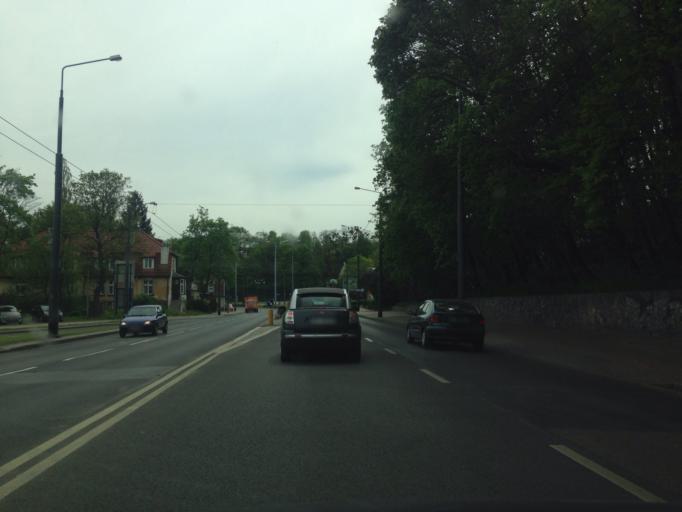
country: PL
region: Pomeranian Voivodeship
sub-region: Sopot
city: Sopot
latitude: 54.4518
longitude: 18.5551
